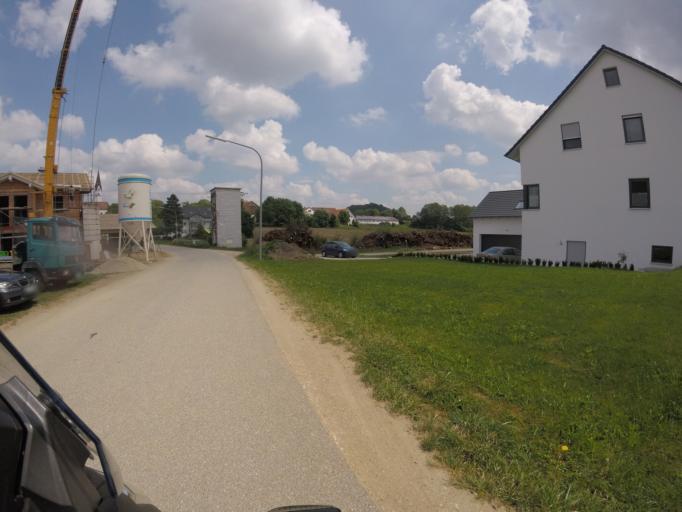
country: DE
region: Bavaria
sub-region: Lower Bavaria
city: Pfeffenhausen
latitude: 48.6769
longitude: 11.9137
